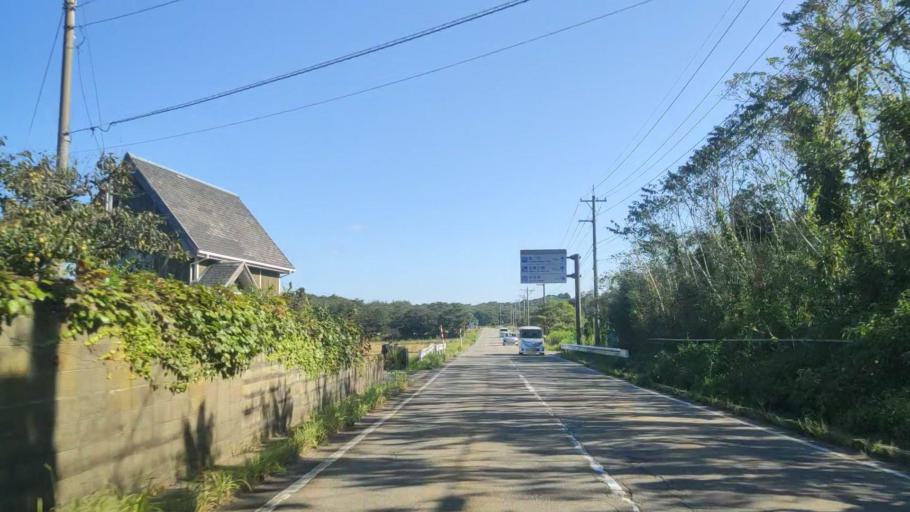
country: JP
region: Ishikawa
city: Hakui
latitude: 36.9581
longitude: 136.7712
